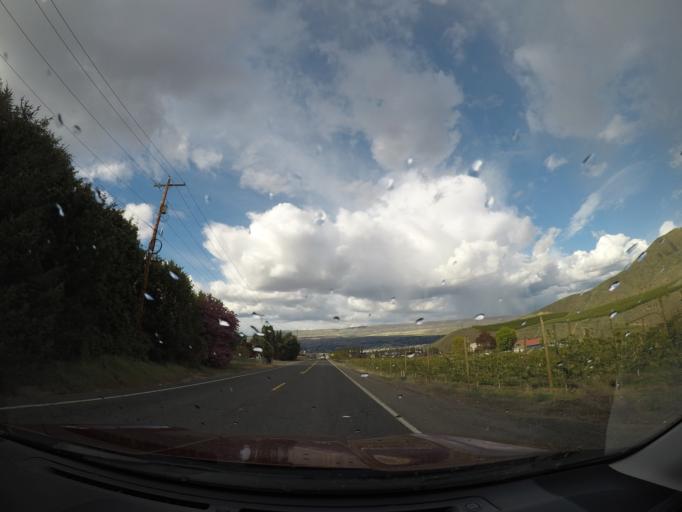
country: US
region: Washington
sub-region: Chelan County
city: South Wenatchee
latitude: 47.3855
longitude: -120.3098
